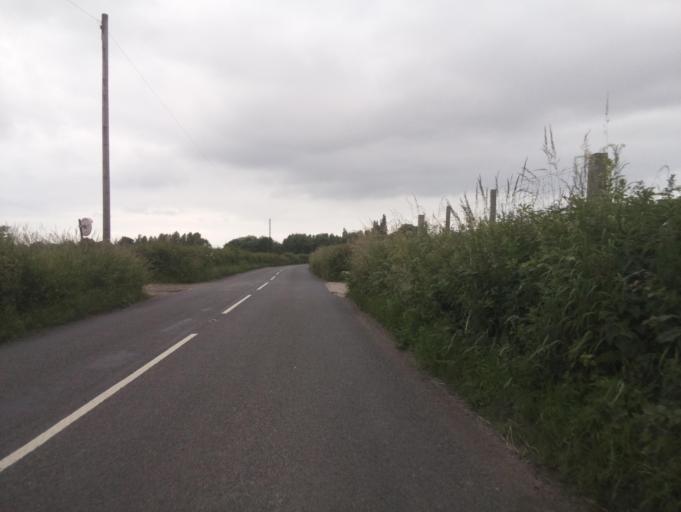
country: GB
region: England
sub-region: Derbyshire
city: Rodsley
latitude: 52.8803
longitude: -1.7493
